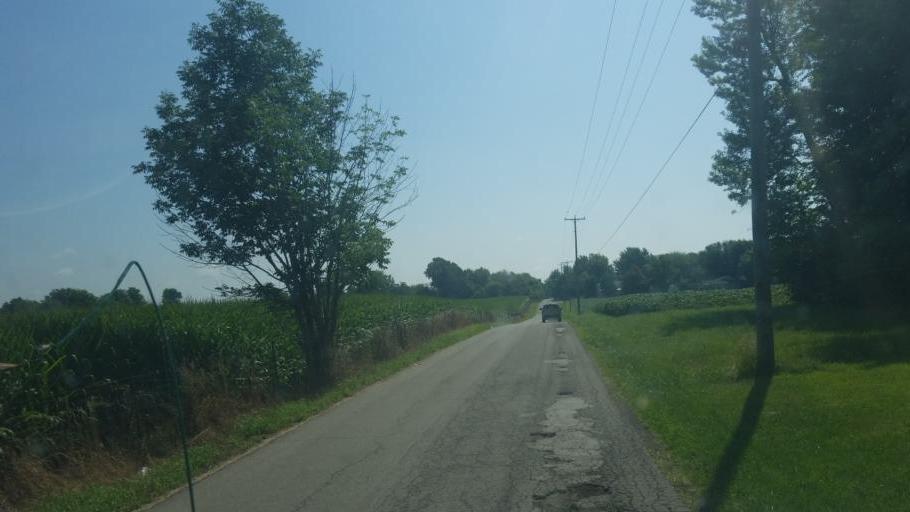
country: US
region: Ohio
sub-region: Hardin County
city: Kenton
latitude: 40.6598
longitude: -83.6158
